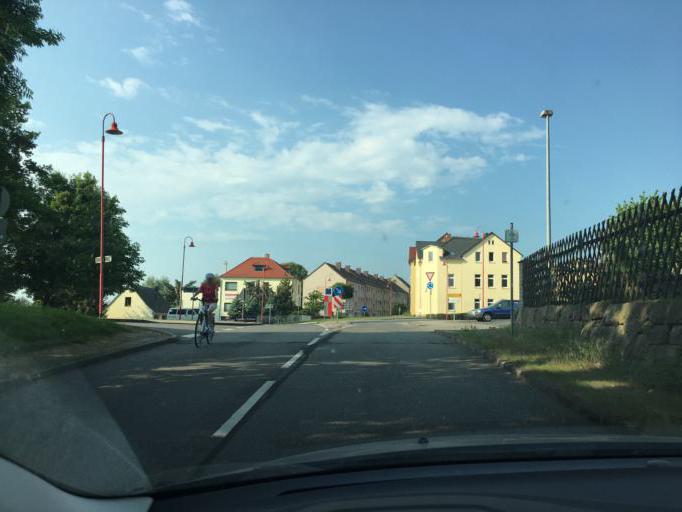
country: DE
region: Saxony
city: Colditz
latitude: 51.1250
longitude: 12.8064
